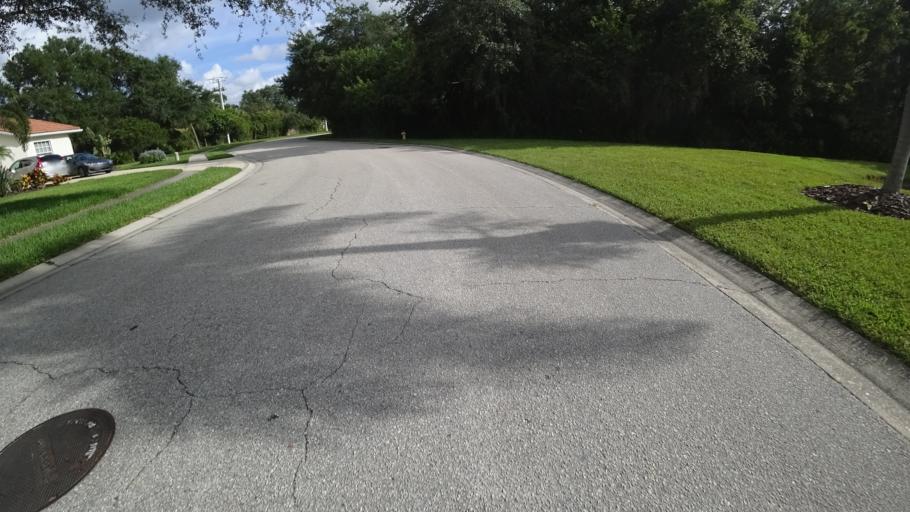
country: US
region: Florida
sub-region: Sarasota County
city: Desoto Lakes
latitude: 27.4134
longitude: -82.4845
